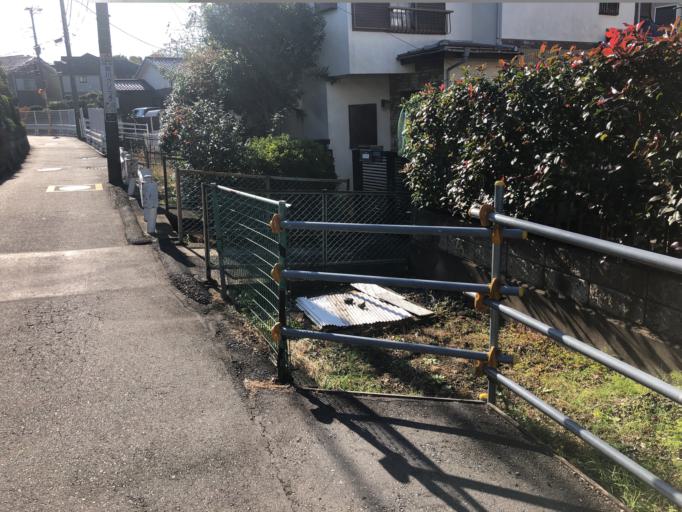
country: JP
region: Kanagawa
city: Chigasaki
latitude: 35.3574
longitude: 139.4045
